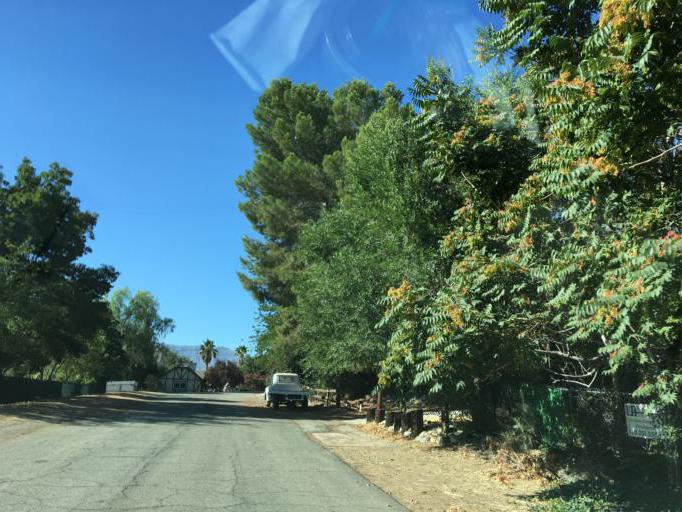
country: US
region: California
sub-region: Los Angeles County
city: Acton
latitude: 34.4687
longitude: -118.2009
